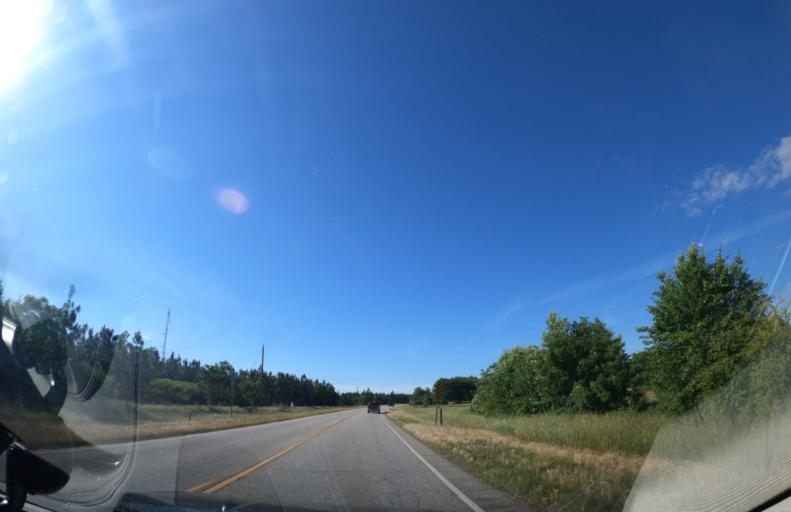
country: US
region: Georgia
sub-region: Columbia County
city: Harlem
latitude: 33.3961
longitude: -82.3141
